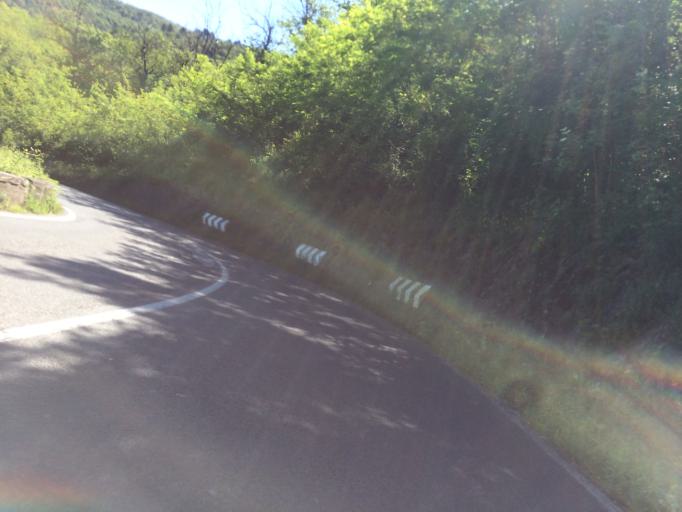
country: IT
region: Tuscany
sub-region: Provincia di Massa-Carrara
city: Albiano Magra
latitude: 44.1836
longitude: 9.9322
